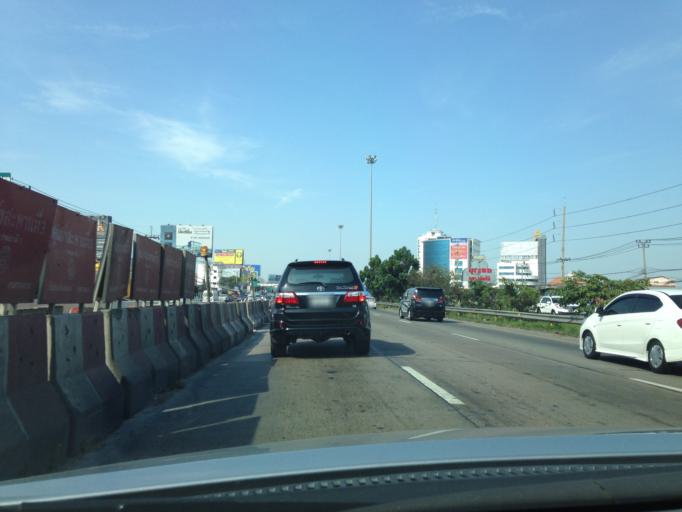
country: TH
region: Nonthaburi
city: Bang Bua Thong
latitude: 13.8653
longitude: 100.4106
